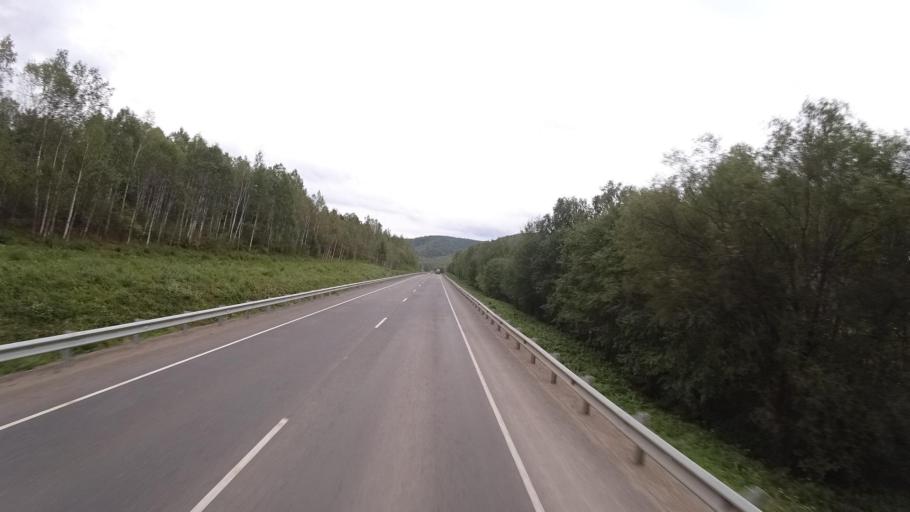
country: RU
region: Jewish Autonomous Oblast
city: Khingansk
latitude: 48.9851
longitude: 131.1419
